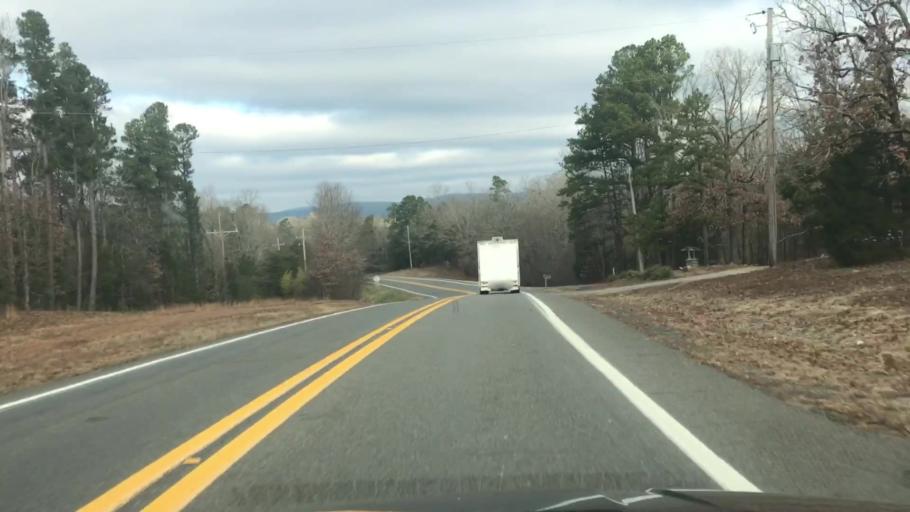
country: US
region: Arkansas
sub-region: Montgomery County
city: Mount Ida
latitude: 34.6202
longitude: -93.7227
